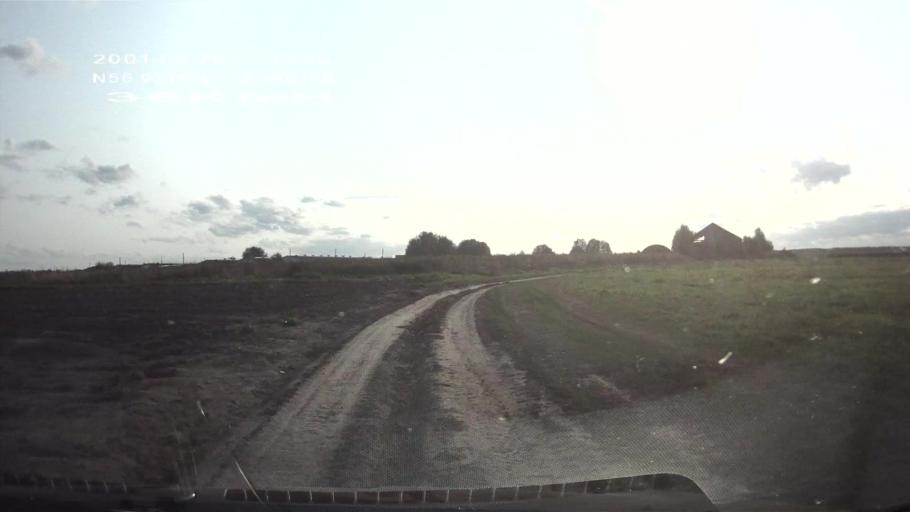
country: RU
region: Mariy-El
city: Kuzhener
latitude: 56.9709
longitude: 48.7892
